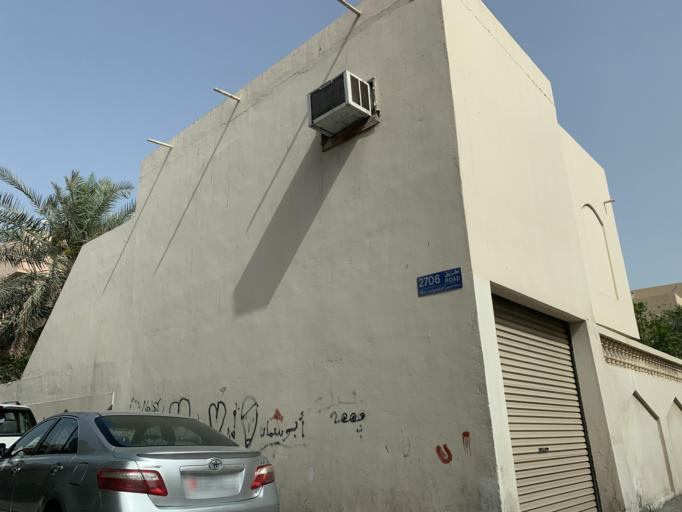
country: BH
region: Northern
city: Ar Rifa'
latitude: 26.1243
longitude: 50.5695
